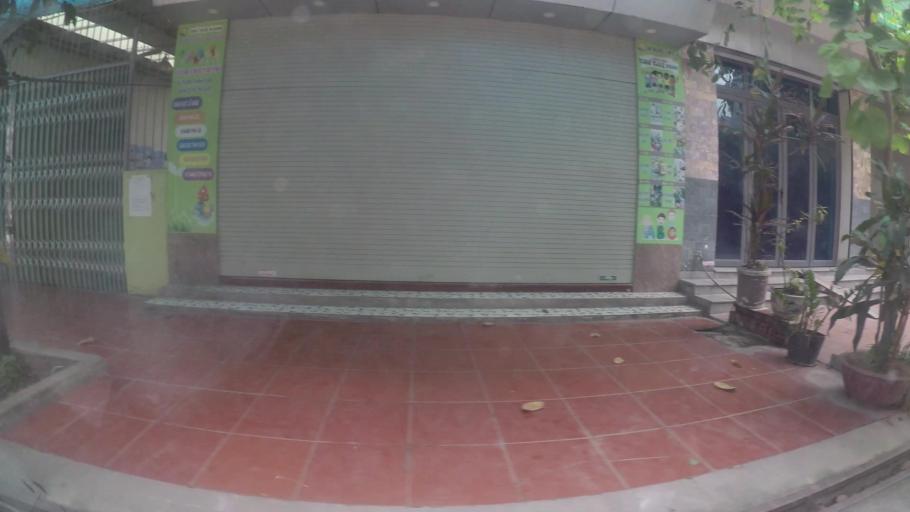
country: VN
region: Ha Noi
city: Ha Dong
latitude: 20.9689
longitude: 105.7696
